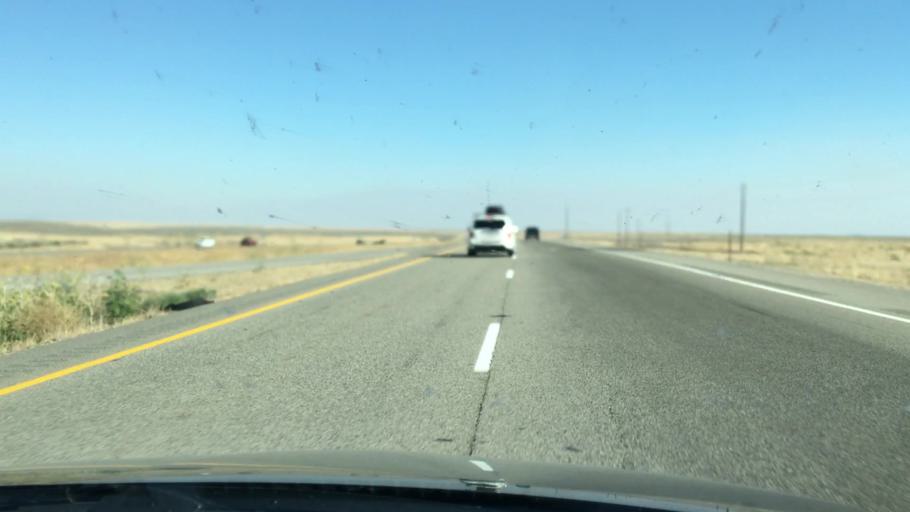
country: US
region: Idaho
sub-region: Ada County
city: Boise
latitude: 43.4683
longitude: -116.0977
